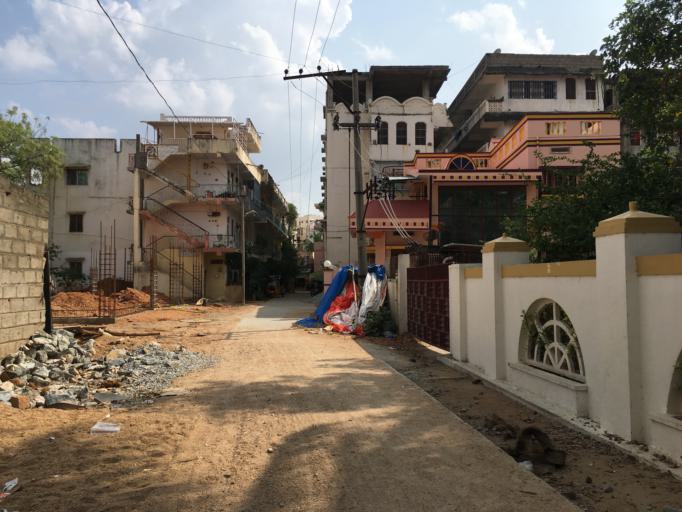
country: IN
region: Andhra Pradesh
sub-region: Anantapur
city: Puttaparthi
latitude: 14.1679
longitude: 77.8141
